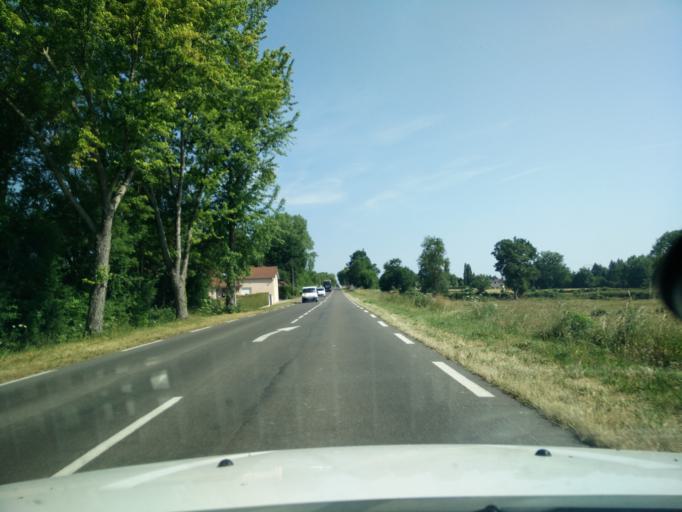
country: FR
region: Auvergne
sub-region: Departement de l'Allier
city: Toulon-sur-Allier
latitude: 46.5080
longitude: 3.3169
